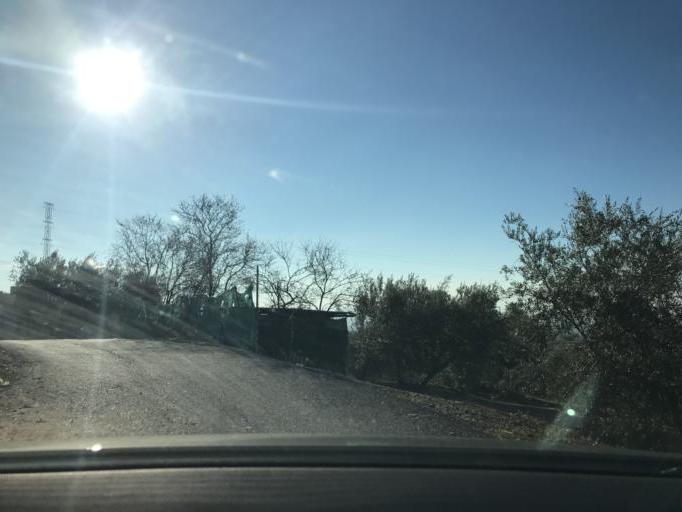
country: ES
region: Andalusia
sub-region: Provincia de Granada
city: Peligros
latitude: 37.2423
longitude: -3.6349
